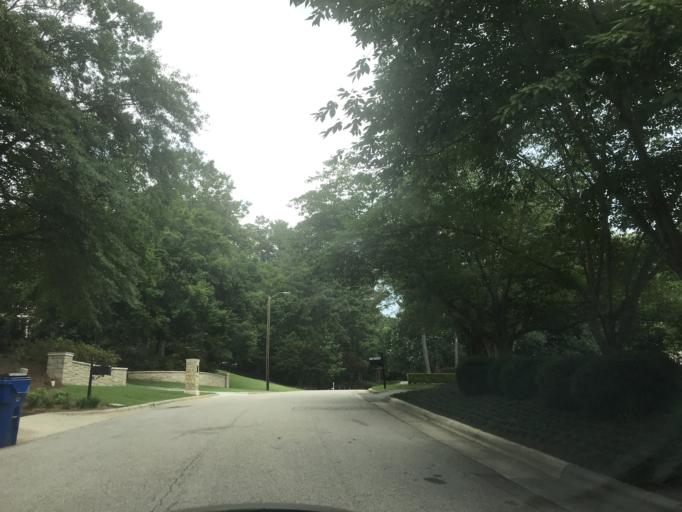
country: US
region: North Carolina
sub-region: Wake County
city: West Raleigh
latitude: 35.8300
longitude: -78.6502
